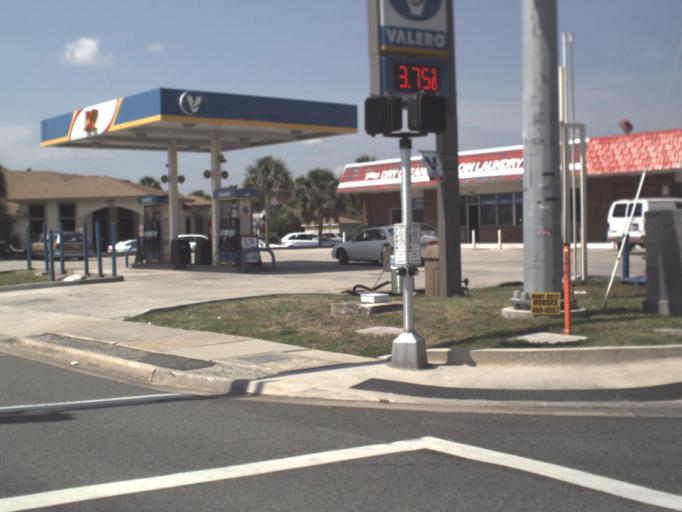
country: US
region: Florida
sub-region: Duval County
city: Jacksonville Beach
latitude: 30.2761
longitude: -81.3894
